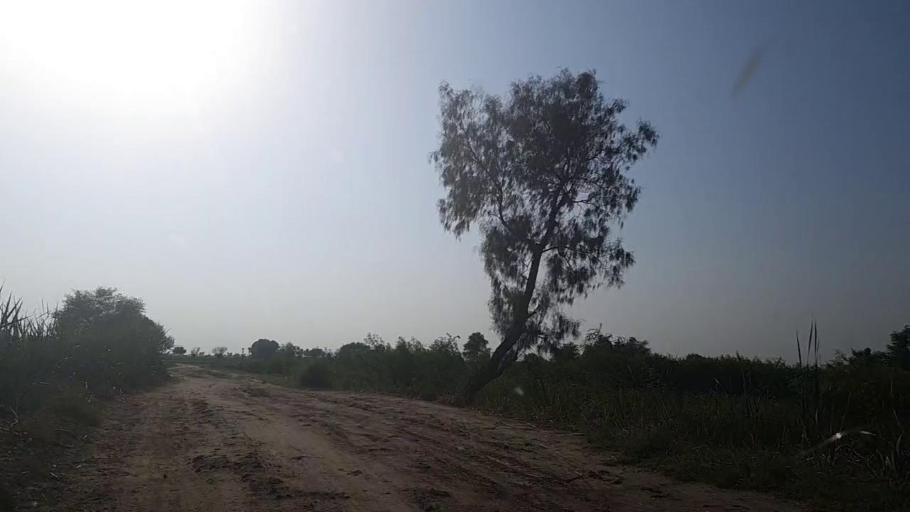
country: PK
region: Sindh
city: Khanpur
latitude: 27.7316
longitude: 69.3249
